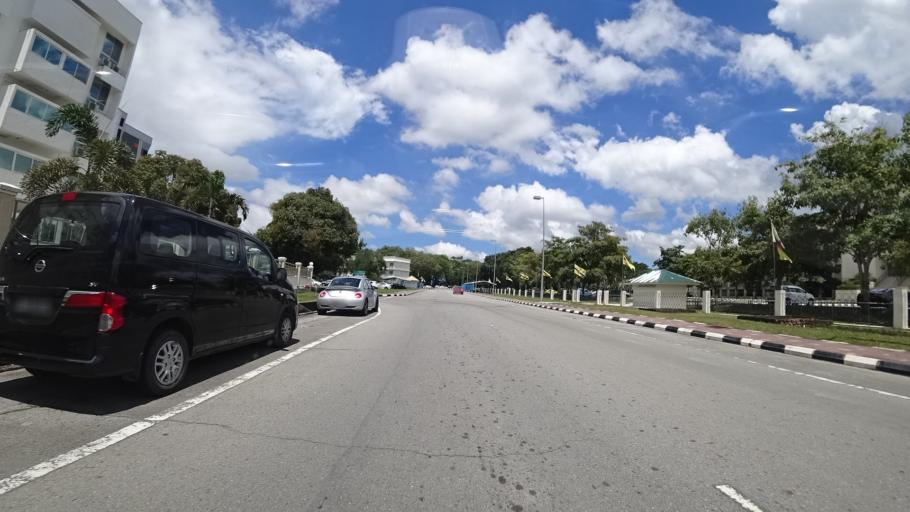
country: BN
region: Brunei and Muara
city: Bandar Seri Begawan
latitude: 4.8928
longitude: 114.9389
